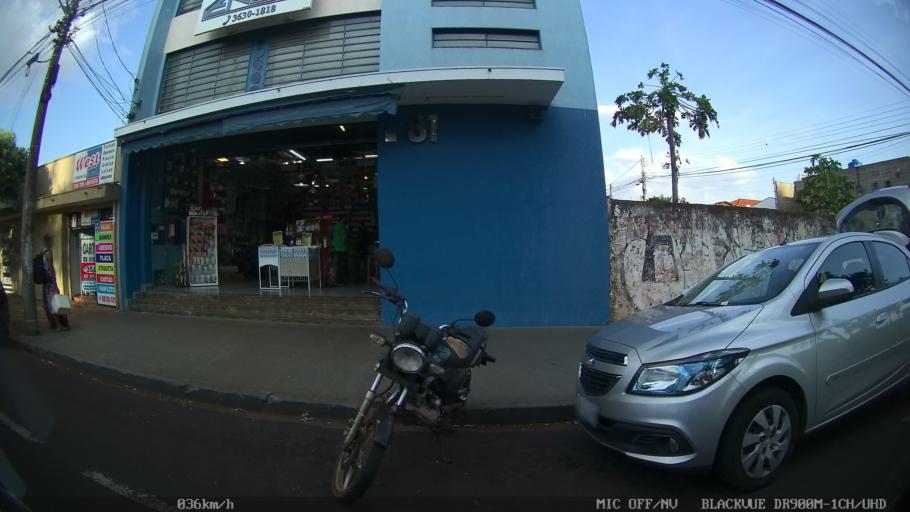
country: BR
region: Sao Paulo
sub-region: Ribeirao Preto
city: Ribeirao Preto
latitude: -21.1676
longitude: -47.8303
